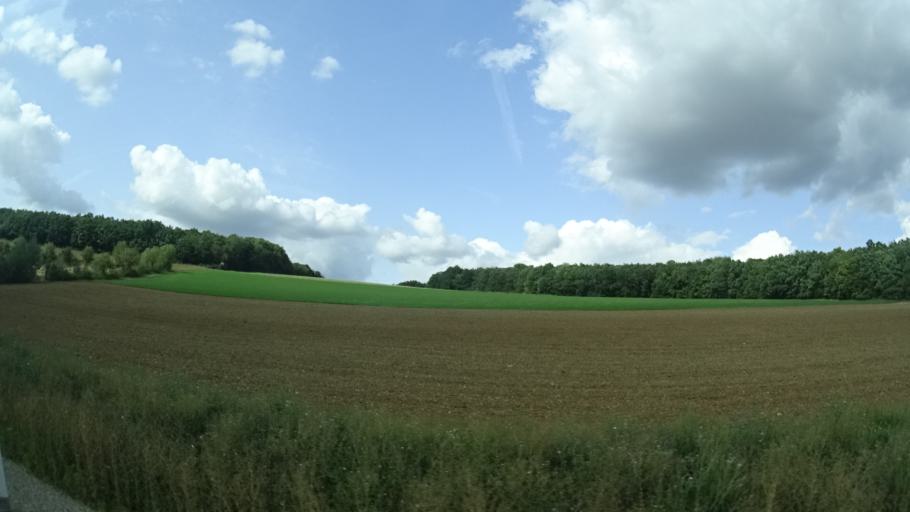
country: DE
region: Bavaria
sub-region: Regierungsbezirk Unterfranken
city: Werneck
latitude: 49.9631
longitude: 10.0373
